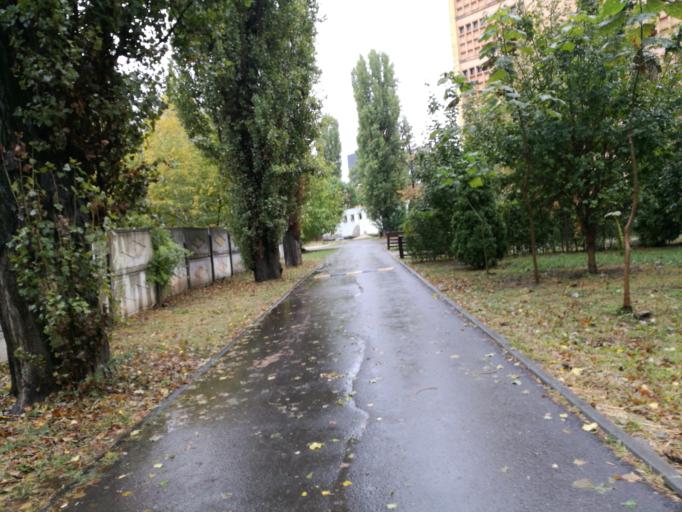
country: RO
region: Ilfov
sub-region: Comuna Chiajna
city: Rosu
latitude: 44.4465
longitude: 26.0531
